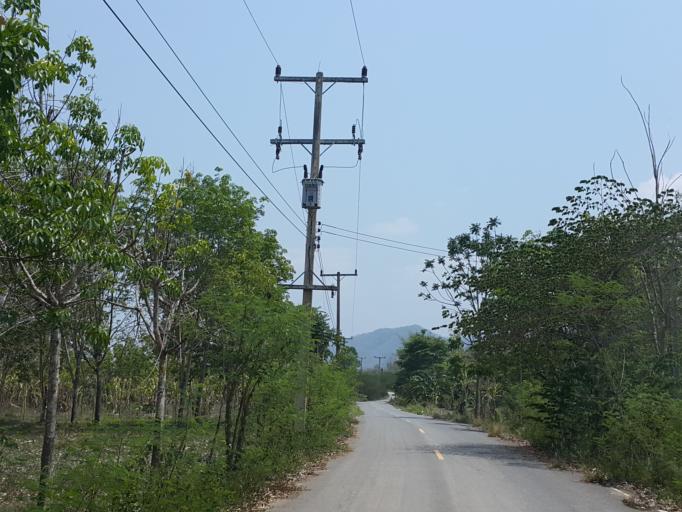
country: TH
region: Kanchanaburi
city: Sai Yok
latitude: 14.1825
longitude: 98.9554
